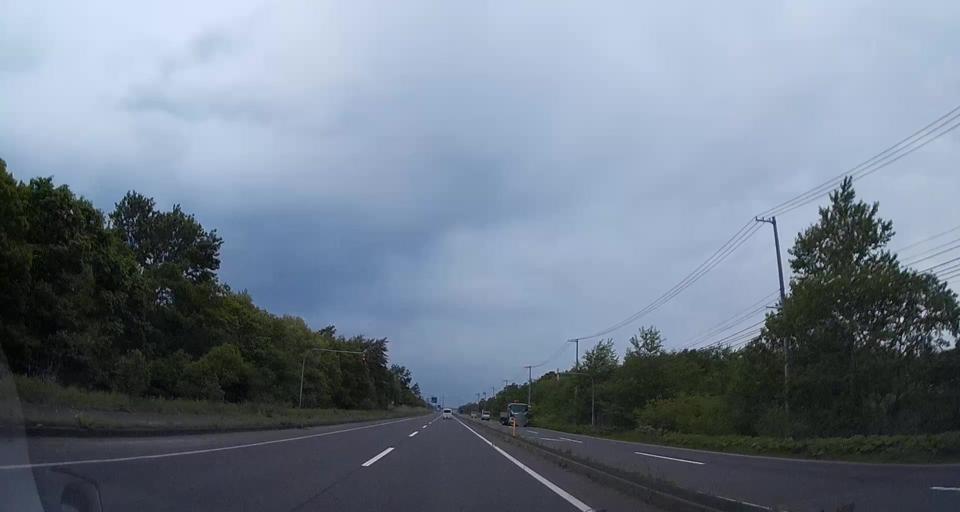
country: JP
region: Hokkaido
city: Tomakomai
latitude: 42.6839
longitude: 141.7205
